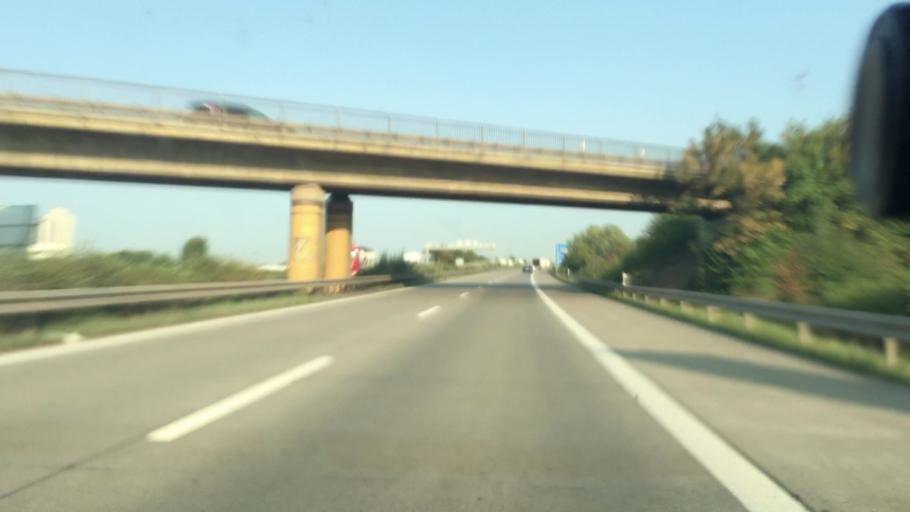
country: DE
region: Saxony-Anhalt
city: Diesdorf
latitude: 52.0641
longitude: 11.5729
